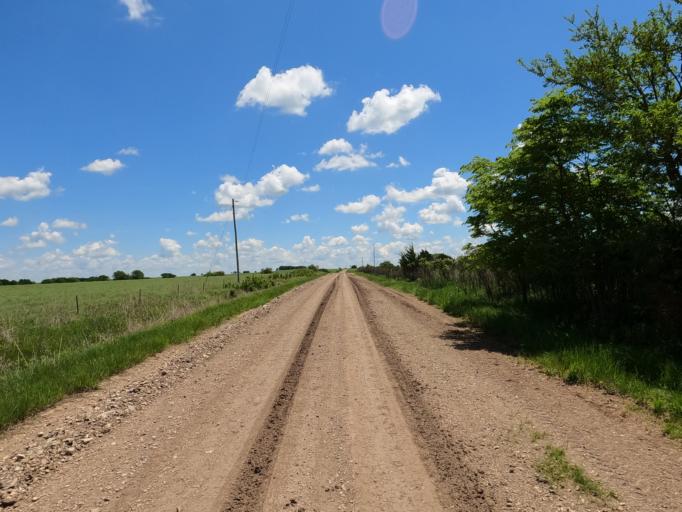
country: US
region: Kansas
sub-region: Marion County
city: Marion
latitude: 38.2165
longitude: -96.7735
